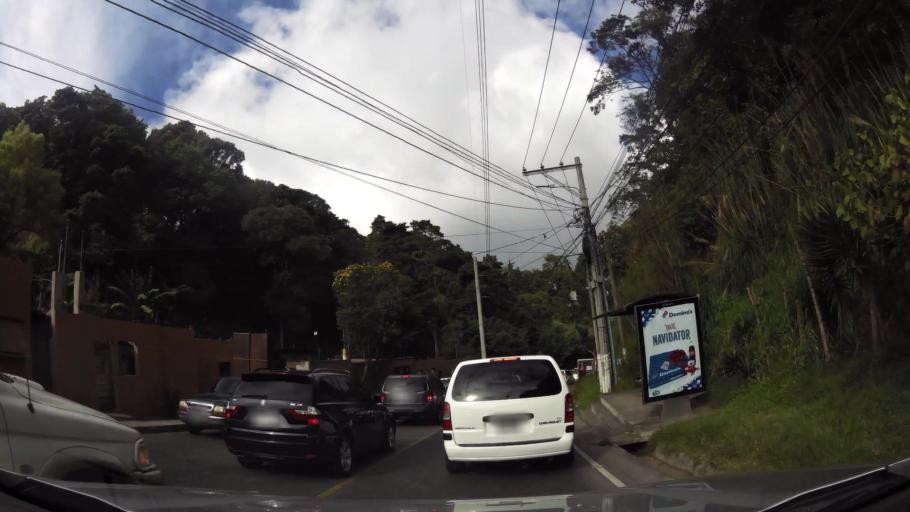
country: GT
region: Guatemala
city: Santa Catarina Pinula
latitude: 14.5646
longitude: -90.4800
